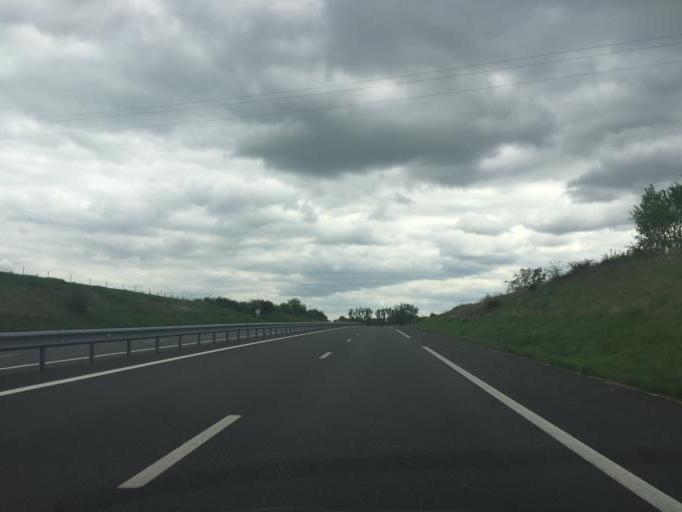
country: FR
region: Rhone-Alpes
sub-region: Departement de la Loire
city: La Pacaudiere
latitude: 46.1756
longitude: 3.8800
